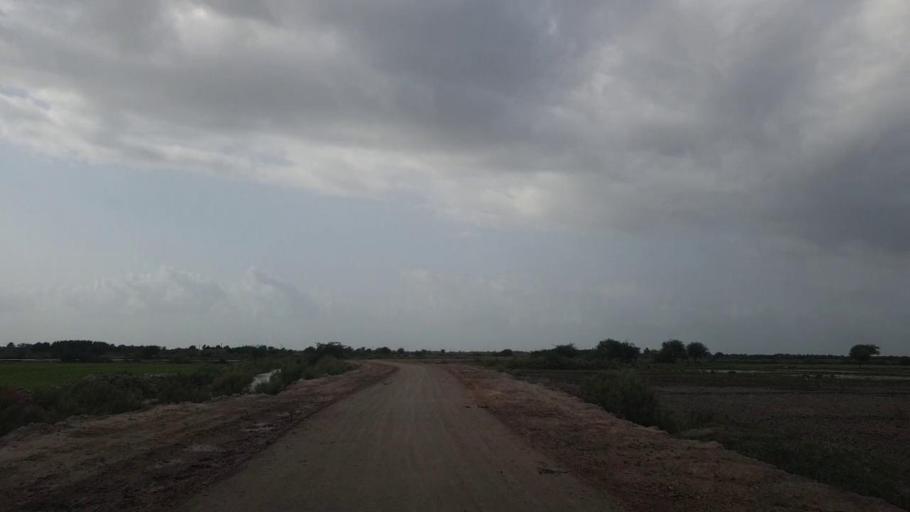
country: PK
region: Sindh
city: Kadhan
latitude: 24.5821
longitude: 69.0573
